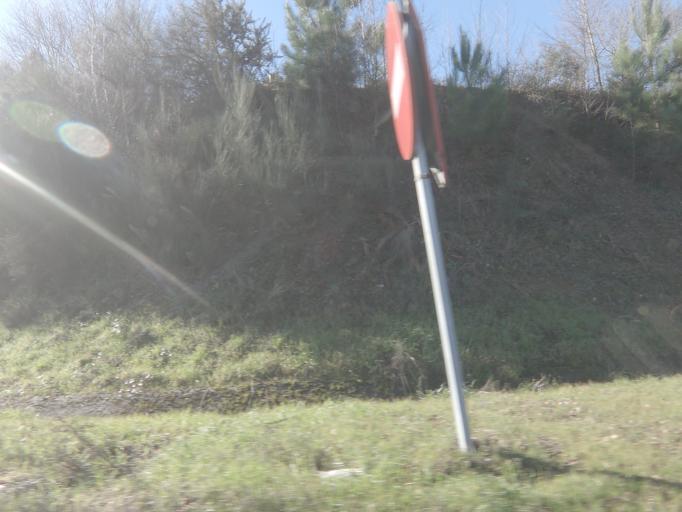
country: ES
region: Galicia
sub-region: Provincia de Pontevedra
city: Lalin
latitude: 42.6738
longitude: -8.1620
